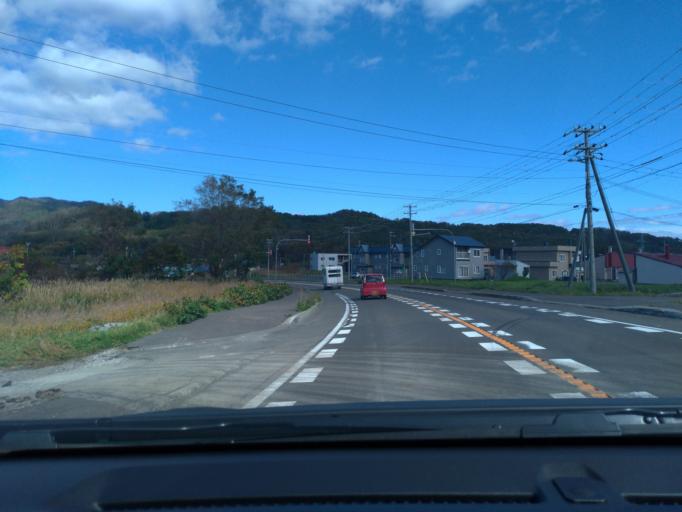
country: JP
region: Hokkaido
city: Ishikari
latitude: 43.3955
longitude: 141.4367
